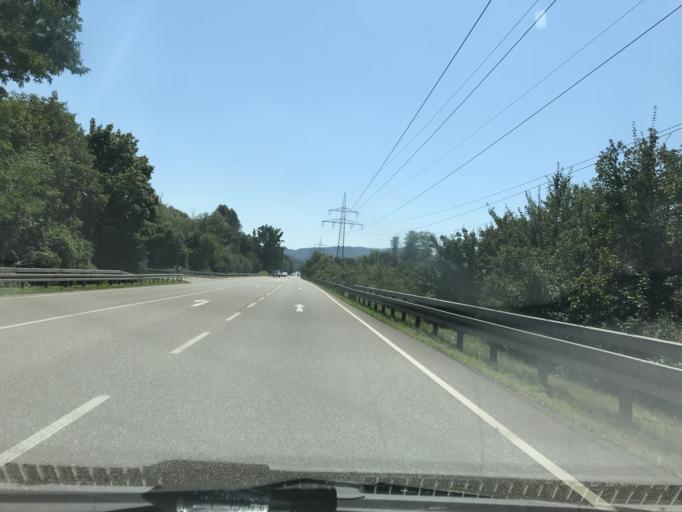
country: CH
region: Aargau
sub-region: Bezirk Rheinfelden
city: Mumpf
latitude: 47.5753
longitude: 7.9143
